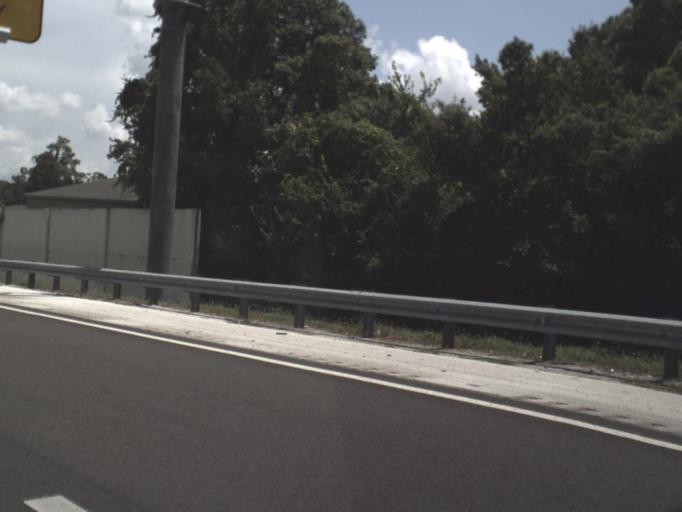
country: US
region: Florida
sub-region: Hillsborough County
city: Plant City
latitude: 28.0276
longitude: -82.1468
